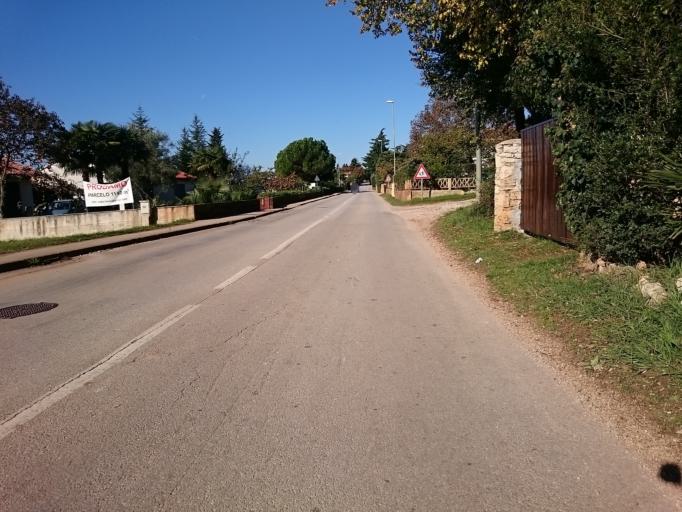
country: HR
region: Istarska
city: Novigrad
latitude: 45.3591
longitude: 13.5559
